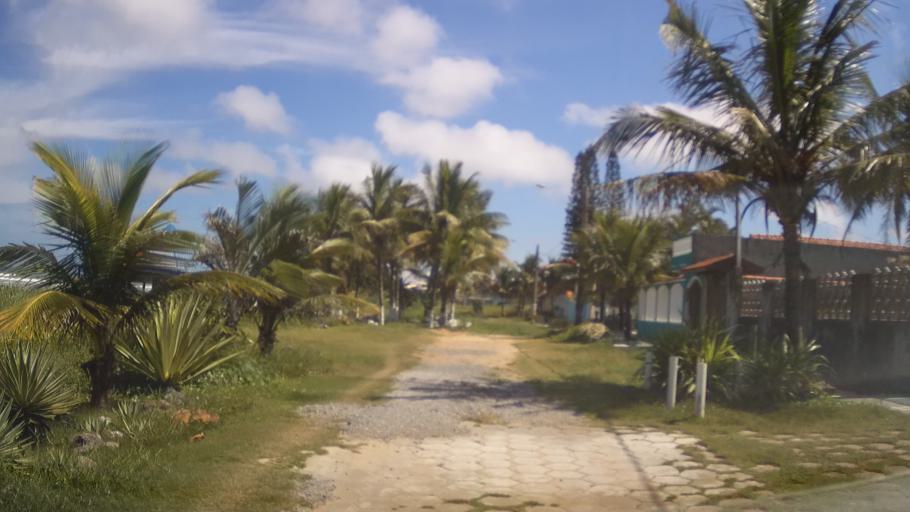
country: BR
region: Sao Paulo
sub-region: Itanhaem
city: Itanhaem
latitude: -24.1469
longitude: -46.7168
